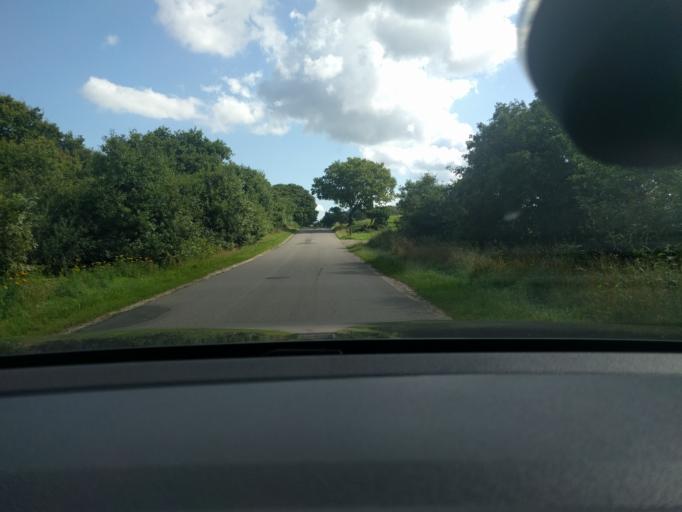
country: DK
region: Central Jutland
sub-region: Viborg Kommune
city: Stoholm
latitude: 56.4882
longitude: 9.2726
